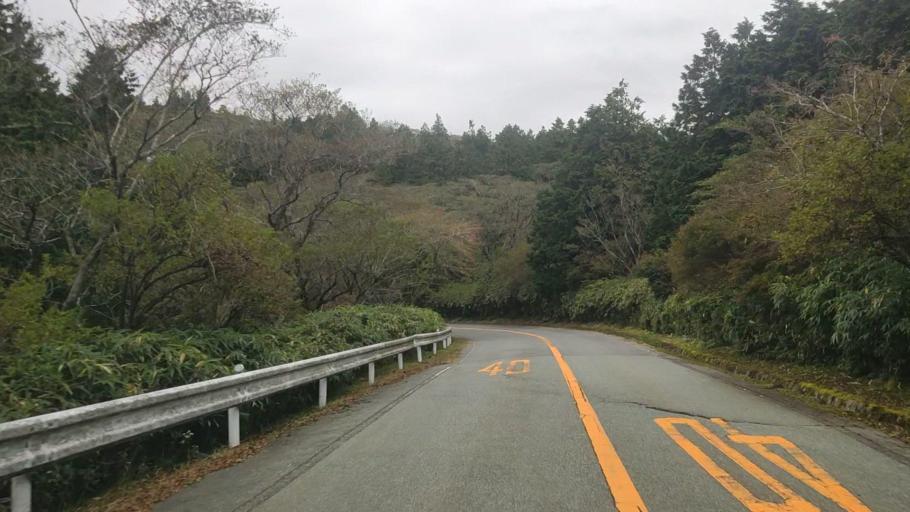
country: JP
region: Shizuoka
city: Heda
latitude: 34.9332
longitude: 138.8337
